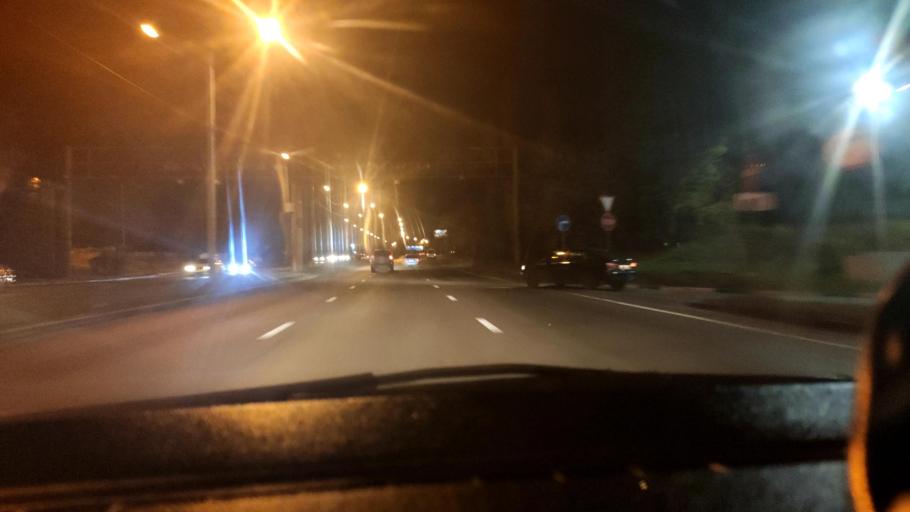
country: RU
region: Voronezj
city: Pridonskoy
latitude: 51.6722
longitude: 39.1198
